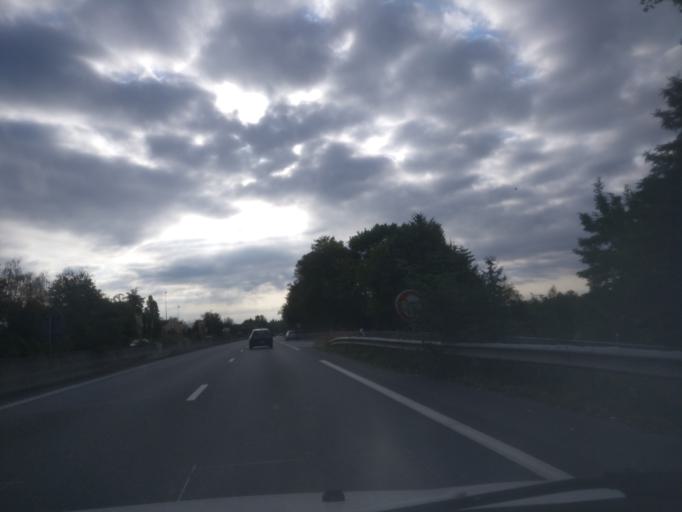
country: FR
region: Pays de la Loire
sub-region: Departement de la Loire-Atlantique
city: Sainte-Luce-sur-Loire
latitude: 47.2464
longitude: -1.5002
